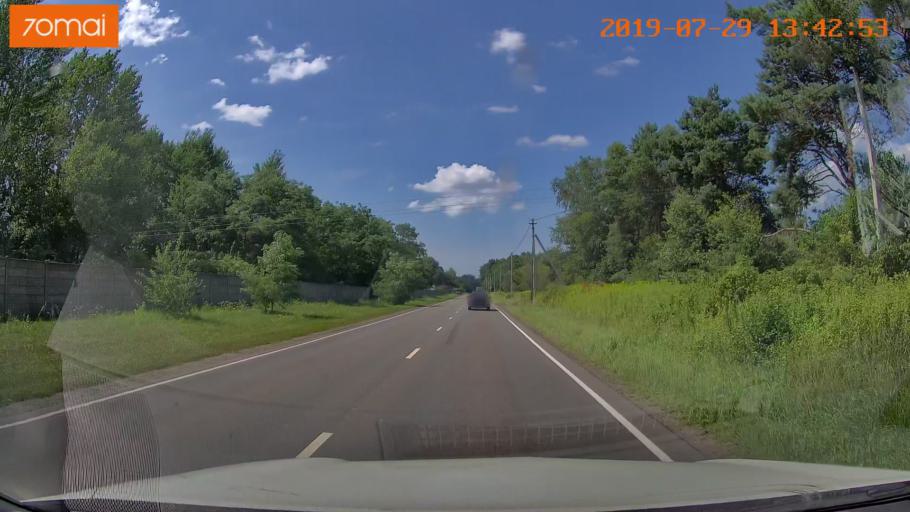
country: RU
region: Kaliningrad
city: Svetlyy
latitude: 54.7370
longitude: 20.1047
